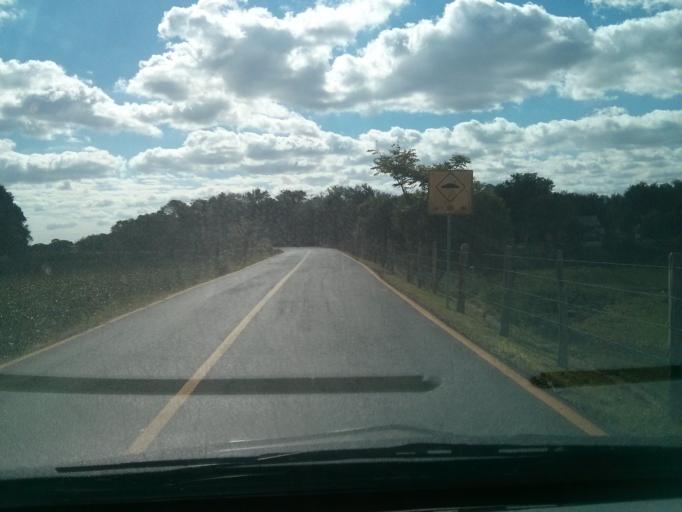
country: BR
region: Parana
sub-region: Sao Jose Dos Pinhais
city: Sao Jose dos Pinhais
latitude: -25.5558
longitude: -49.2262
